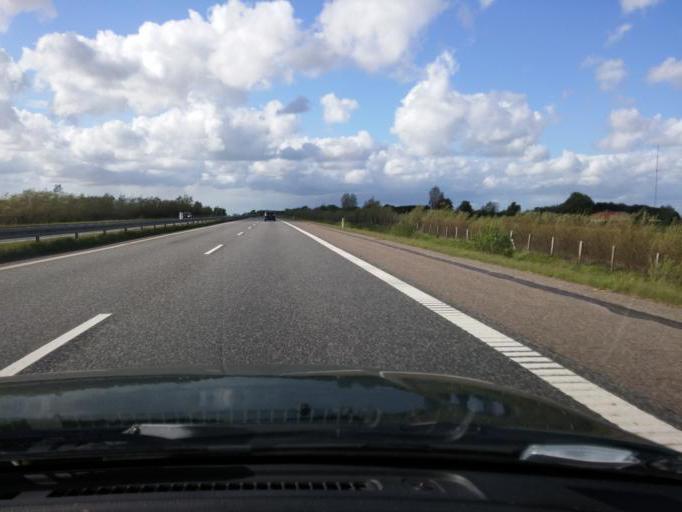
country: DK
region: South Denmark
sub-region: Faaborg-Midtfyn Kommune
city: Ringe
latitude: 55.2670
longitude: 10.4669
